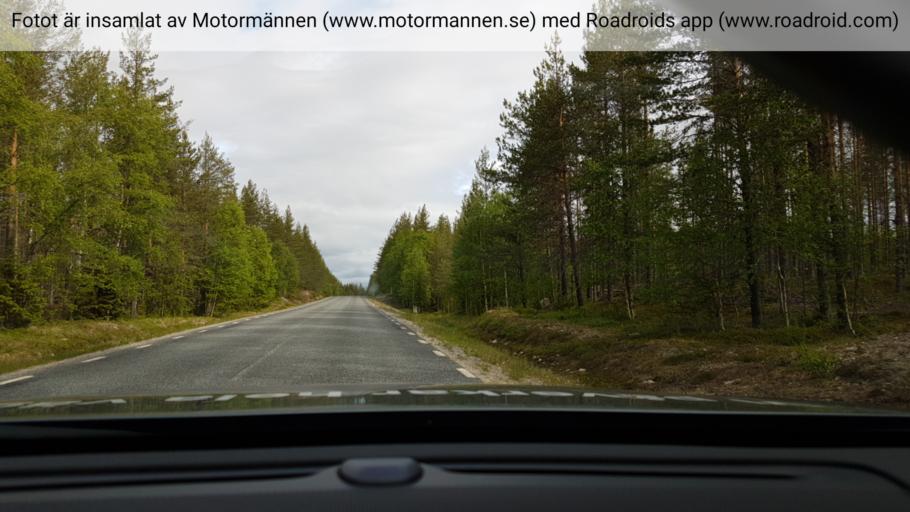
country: SE
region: Vaesterbotten
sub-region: Asele Kommun
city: Insjon
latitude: 64.2383
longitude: 17.5495
